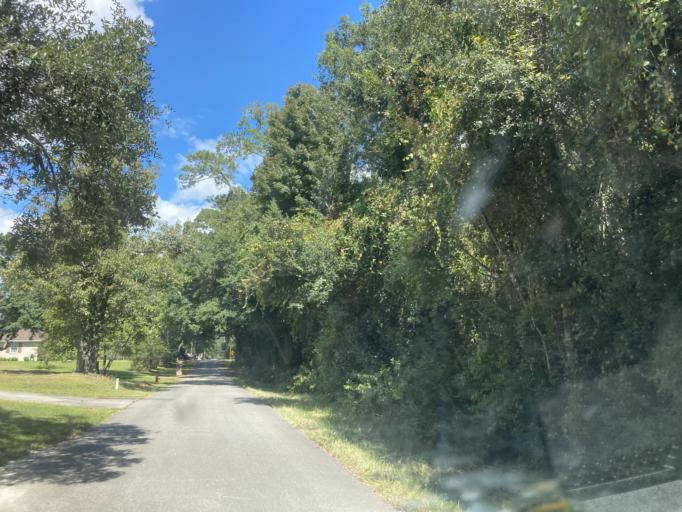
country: US
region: Mississippi
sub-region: Jackson County
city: Gulf Hills
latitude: 30.4446
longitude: -88.8424
